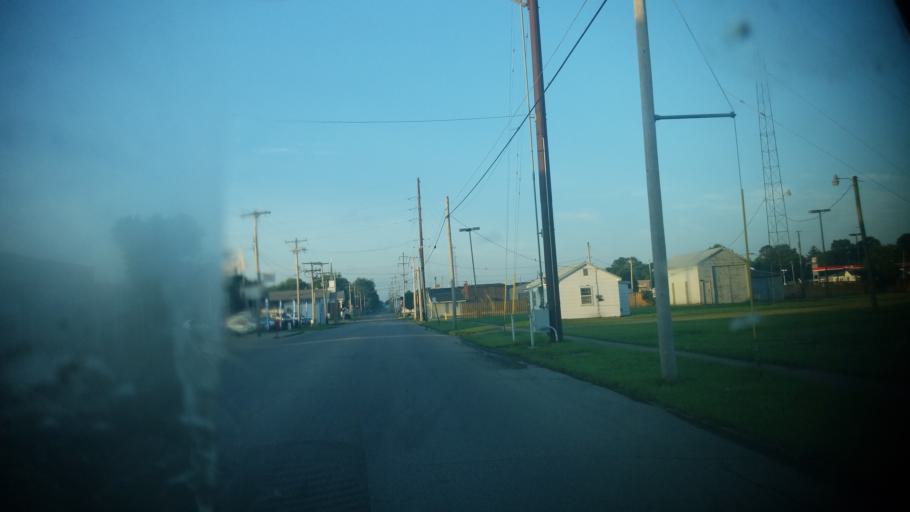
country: US
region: Illinois
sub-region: Wayne County
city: Fairfield
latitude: 38.3810
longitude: -88.3685
